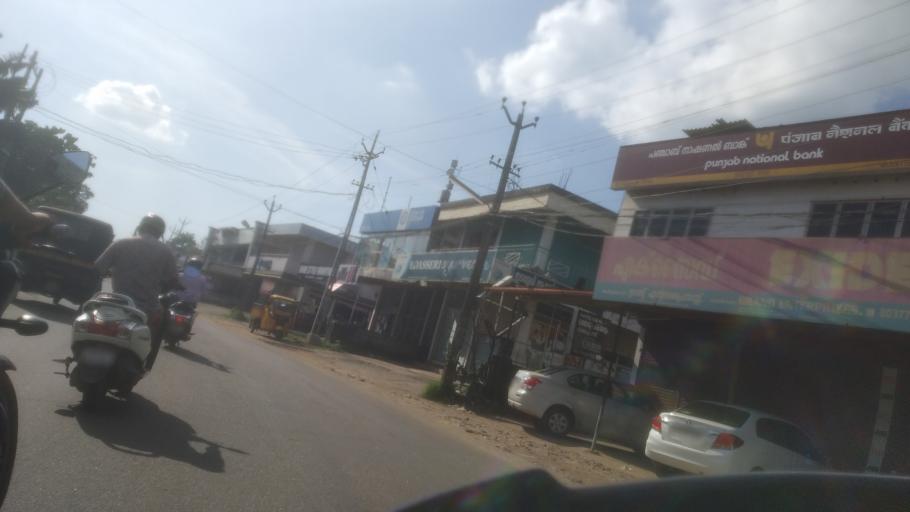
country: IN
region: Kerala
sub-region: Ernakulam
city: Muvattupula
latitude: 9.9929
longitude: 76.5844
